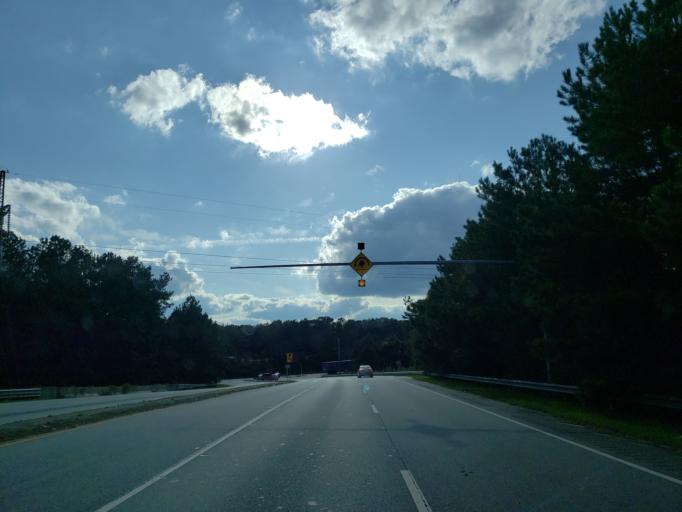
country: US
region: Georgia
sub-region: Cobb County
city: Austell
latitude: 33.8199
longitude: -84.6548
